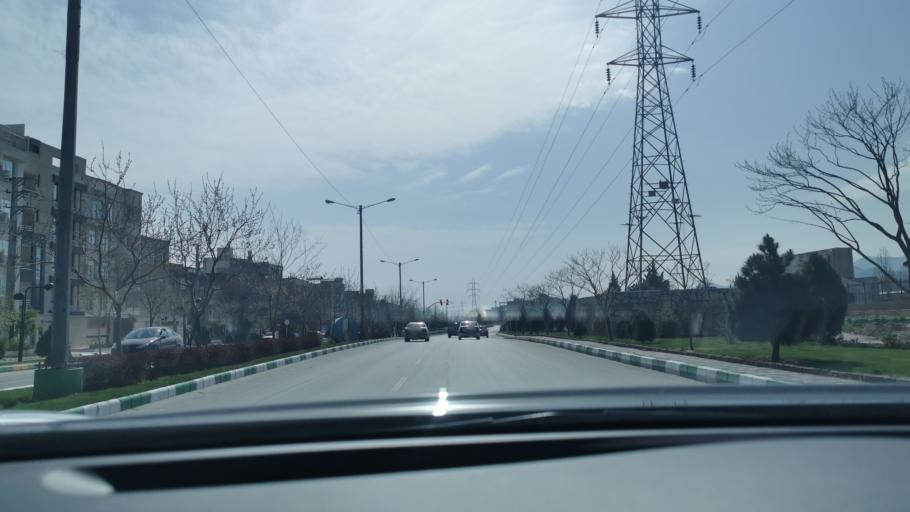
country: IR
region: Razavi Khorasan
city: Mashhad
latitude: 36.2857
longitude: 59.5392
